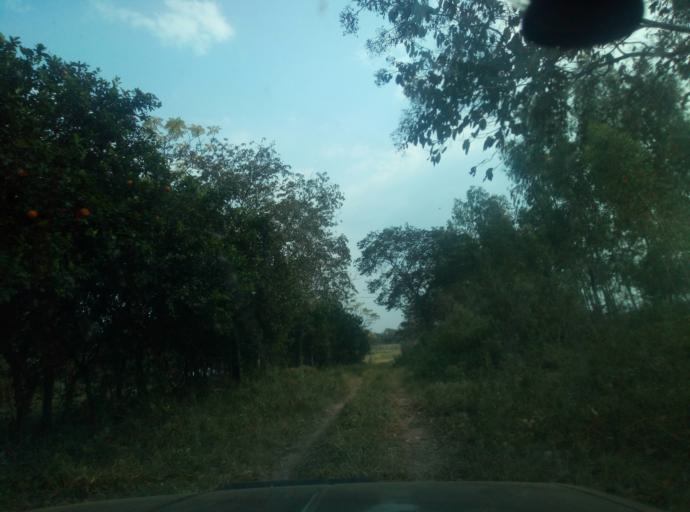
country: PY
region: Caaguazu
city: Doctor Cecilio Baez
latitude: -25.1822
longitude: -56.1342
